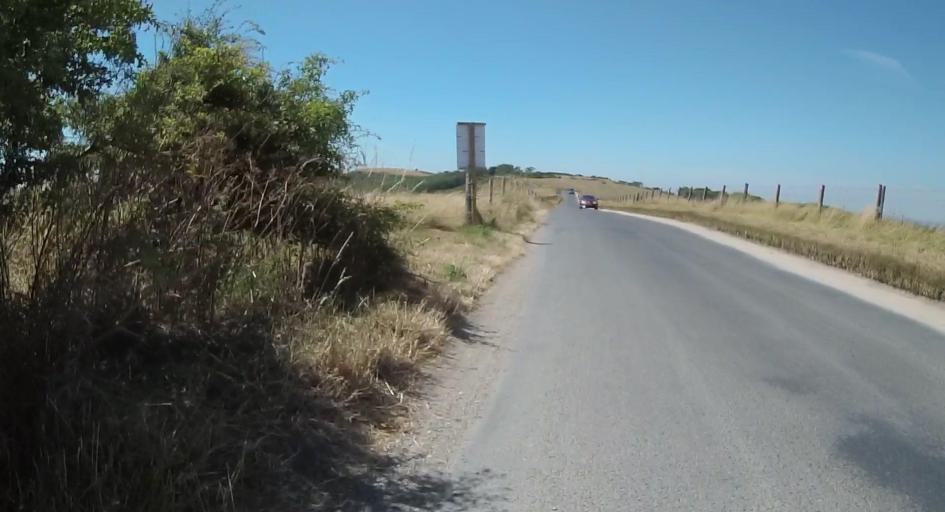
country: GB
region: England
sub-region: Dorset
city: Wareham
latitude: 50.6349
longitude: -2.1378
